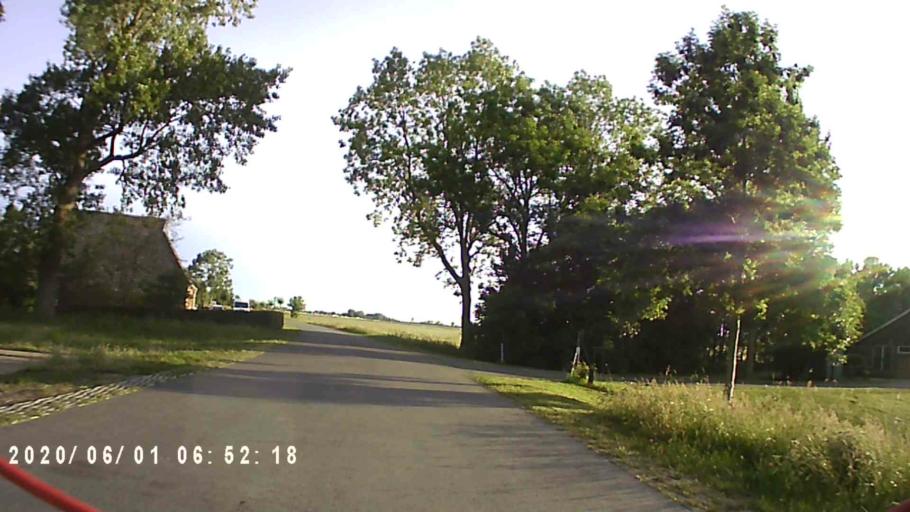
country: NL
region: Friesland
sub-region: Gemeente Kollumerland en Nieuwkruisland
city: Kollum
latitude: 53.3082
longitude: 6.1313
